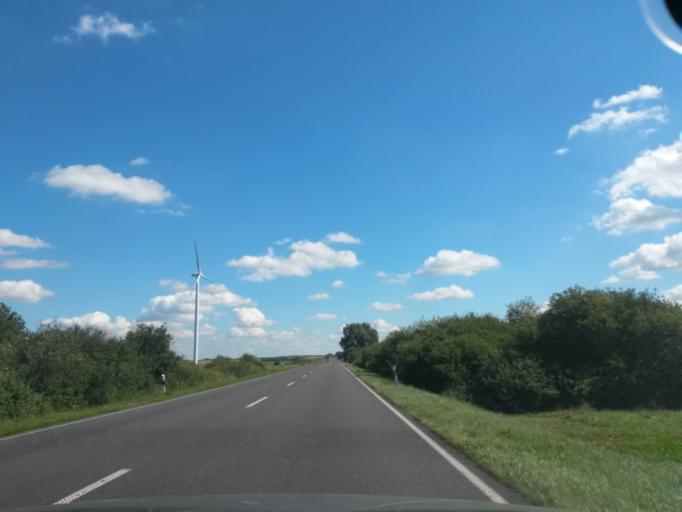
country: DE
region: Brandenburg
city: Pinnow
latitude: 53.0278
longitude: 14.0651
